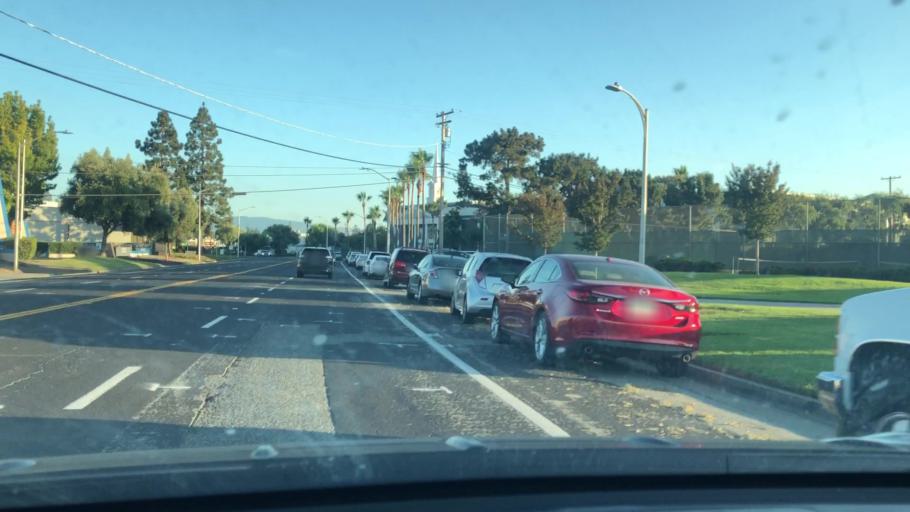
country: US
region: California
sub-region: Santa Clara County
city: Santa Clara
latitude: 37.3884
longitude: -121.9442
